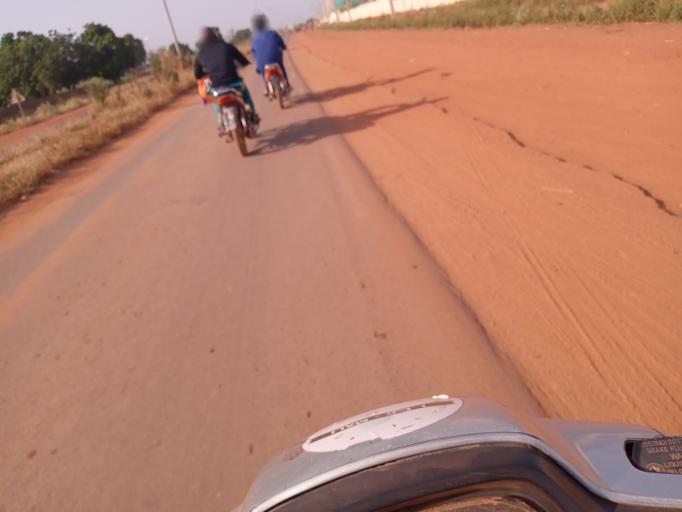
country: ML
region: Bamako
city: Bamako
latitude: 12.4844
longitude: -8.0563
